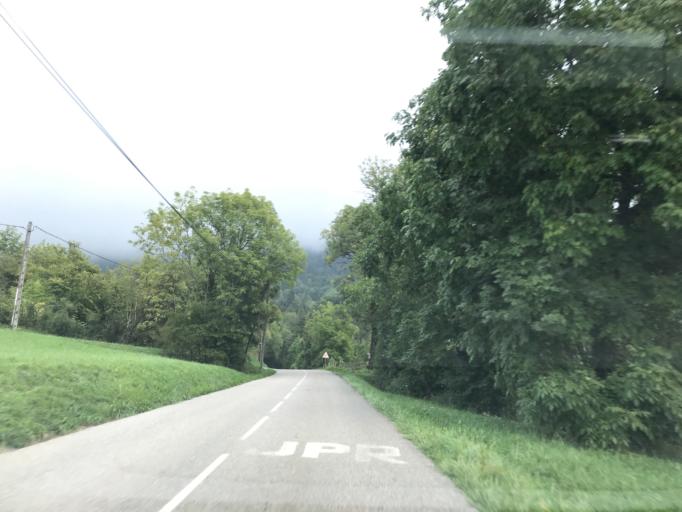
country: FR
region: Rhone-Alpes
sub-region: Departement de la Haute-Savoie
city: Talloires
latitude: 45.8337
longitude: 6.2376
